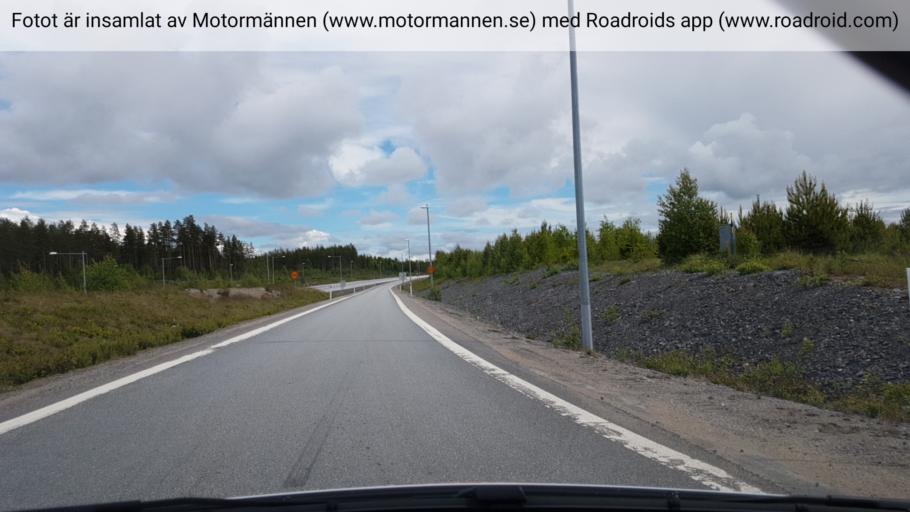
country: SE
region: Vaesterbotten
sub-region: Nordmalings Kommun
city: Nordmaling
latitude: 63.5793
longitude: 19.4864
